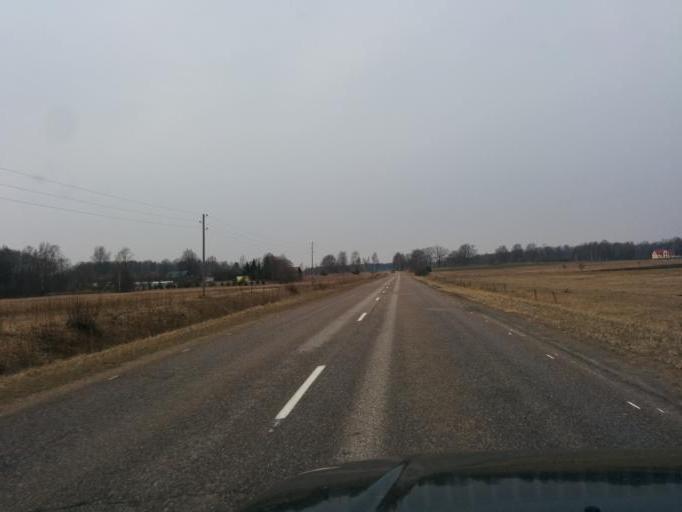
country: LV
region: Ikskile
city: Ikskile
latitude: 56.8189
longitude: 24.4577
